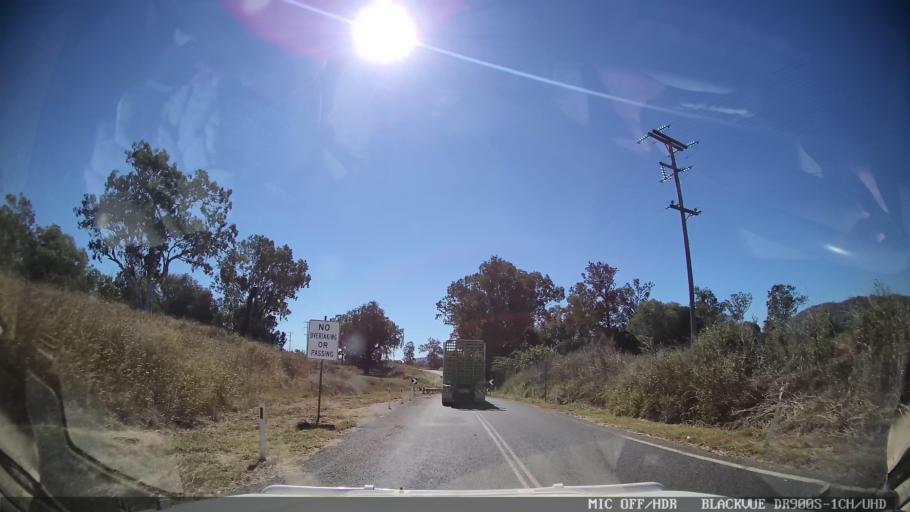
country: AU
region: Queensland
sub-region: Gladstone
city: Toolooa
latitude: -24.2749
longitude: 151.2760
